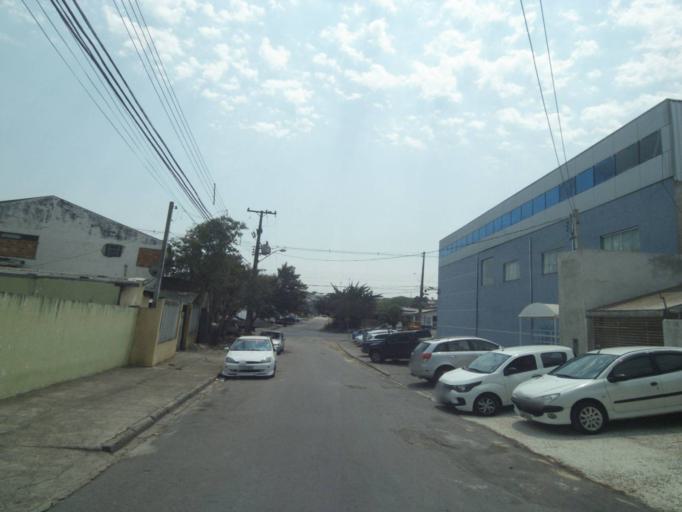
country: BR
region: Parana
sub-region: Sao Jose Dos Pinhais
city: Sao Jose dos Pinhais
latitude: -25.5360
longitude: -49.2503
